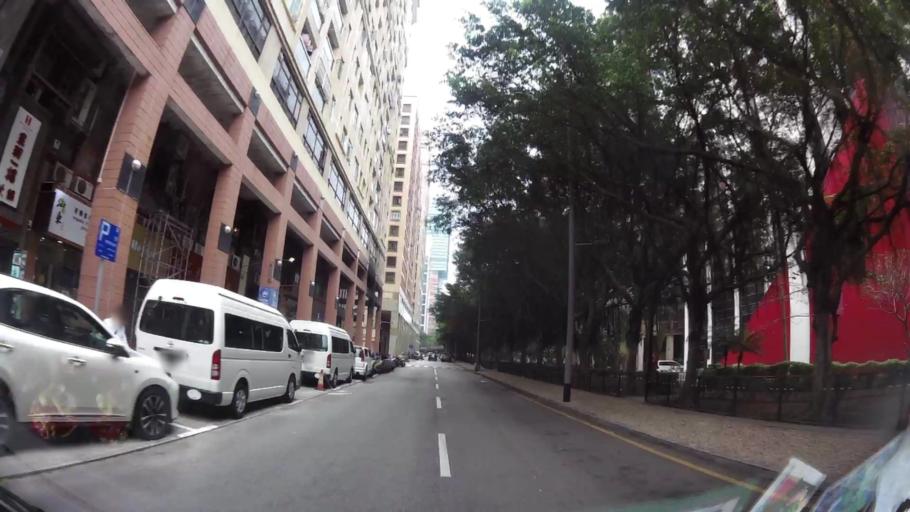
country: MO
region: Macau
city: Macau
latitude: 22.1915
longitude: 113.5523
